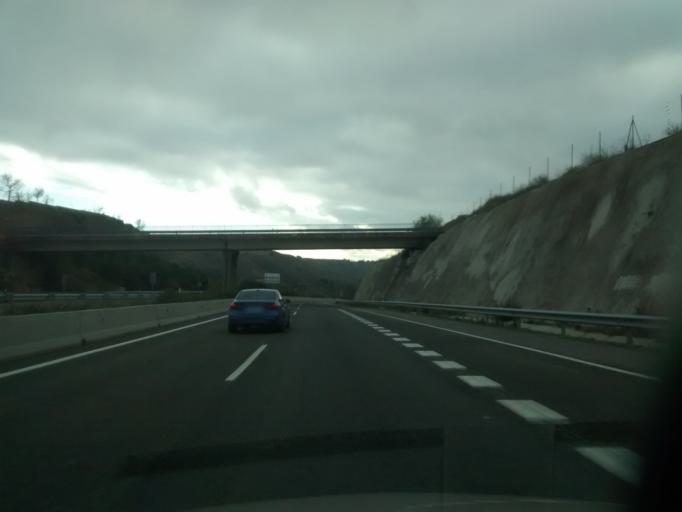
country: ES
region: Castille-La Mancha
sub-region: Provincia de Guadalajara
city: Torija
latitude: 40.7441
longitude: -3.0346
